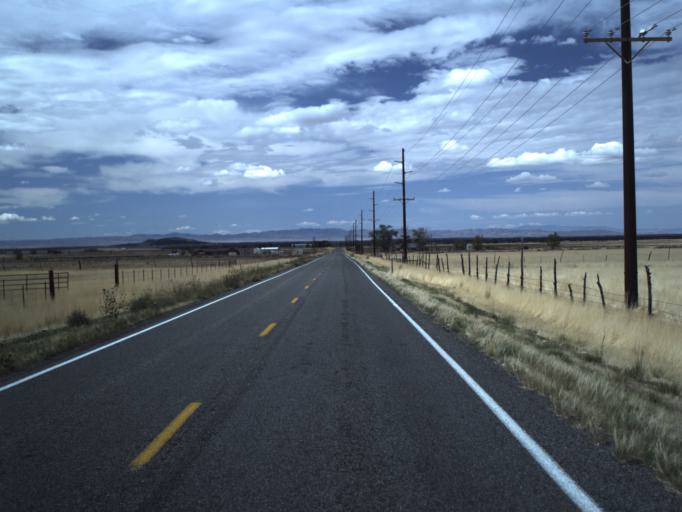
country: US
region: Utah
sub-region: Millard County
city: Fillmore
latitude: 38.9792
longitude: -112.3942
